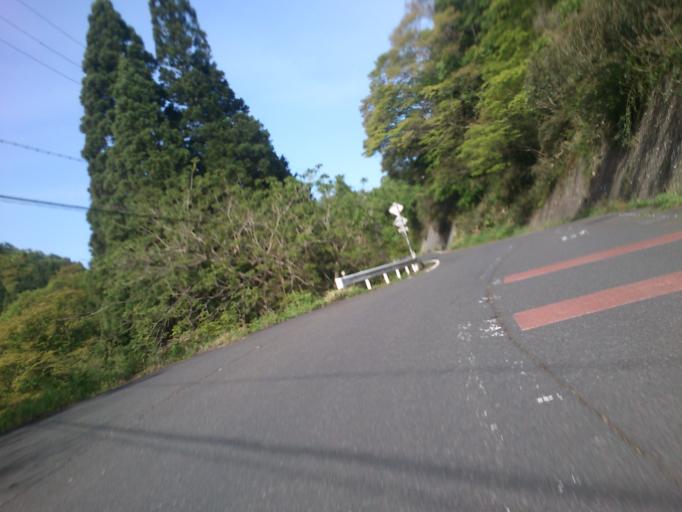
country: JP
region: Kyoto
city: Miyazu
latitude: 35.6350
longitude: 135.2008
